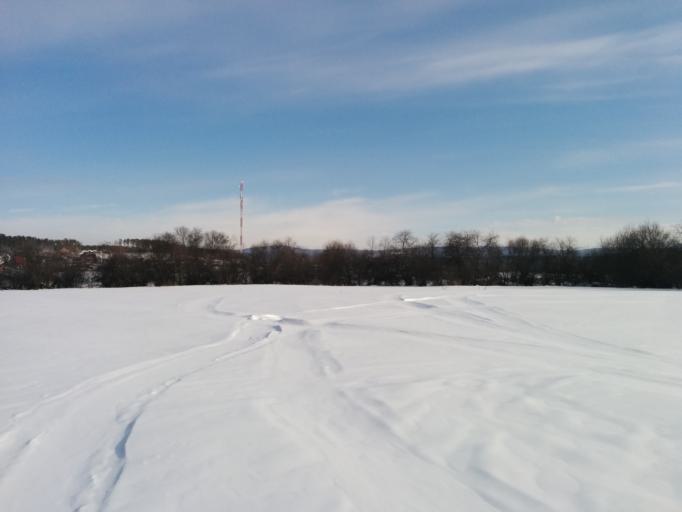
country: RU
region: Bashkortostan
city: Lomovka
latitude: 53.8706
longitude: 58.2574
